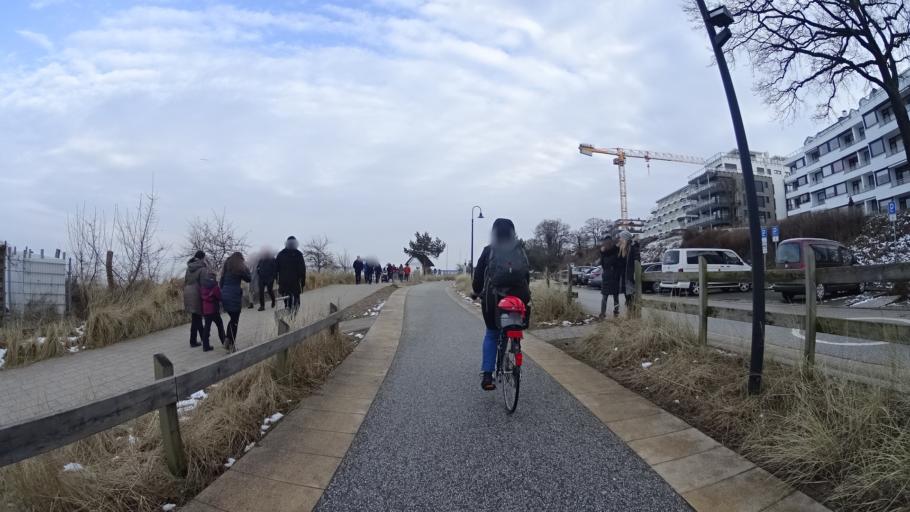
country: DE
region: Schleswig-Holstein
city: Scharbeutz
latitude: 54.0244
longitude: 10.7592
